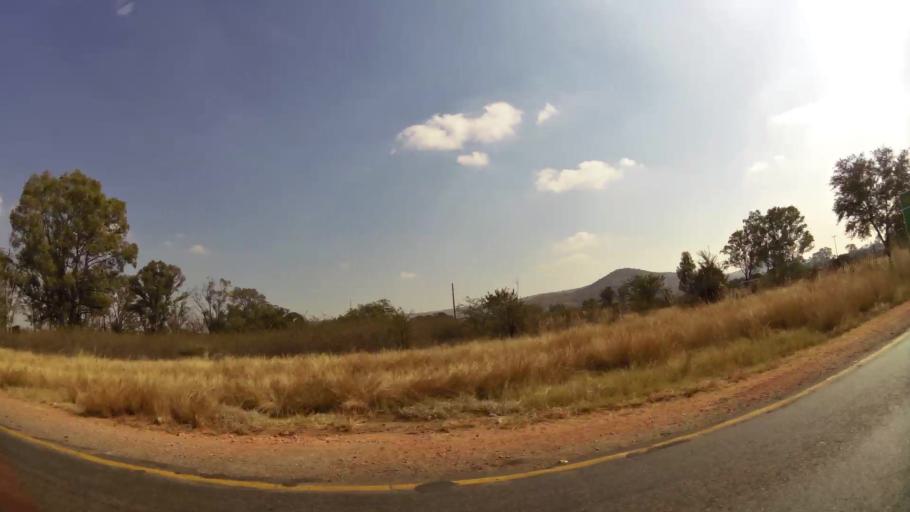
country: ZA
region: North-West
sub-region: Bojanala Platinum District Municipality
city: Rustenburg
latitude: -25.5088
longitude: 27.0995
